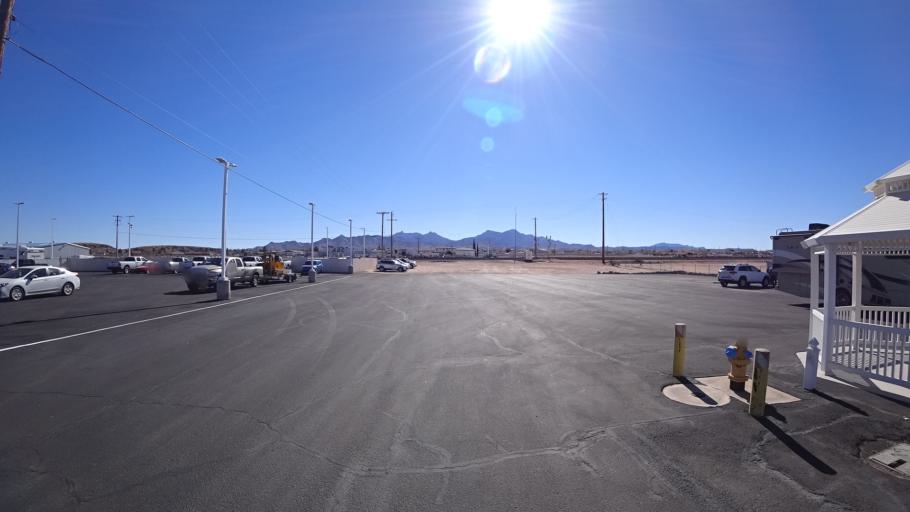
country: US
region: Arizona
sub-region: Mohave County
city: Kingman
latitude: 35.2074
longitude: -114.0190
